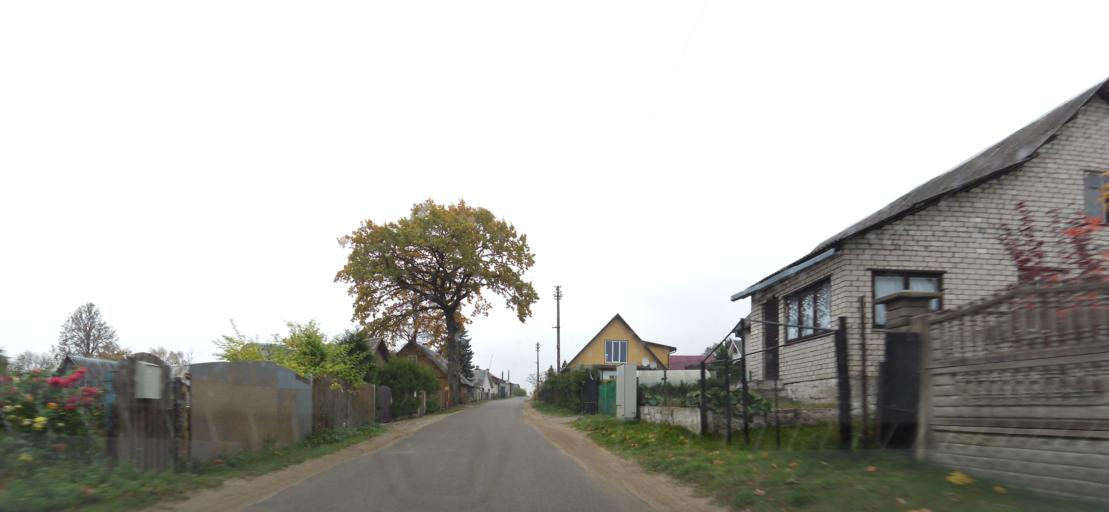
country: BY
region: Grodnenskaya
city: Astravyets
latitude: 54.6365
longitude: 25.6844
